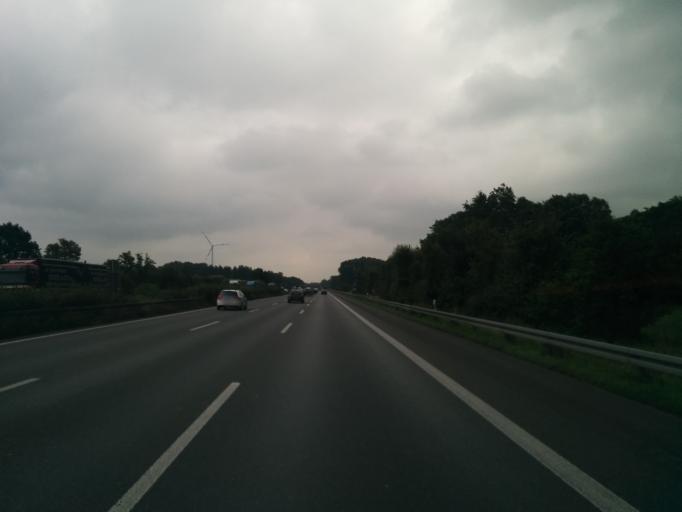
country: DE
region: North Rhine-Westphalia
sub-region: Regierungsbezirk Detmold
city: Guetersloh
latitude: 51.8704
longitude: 8.3918
